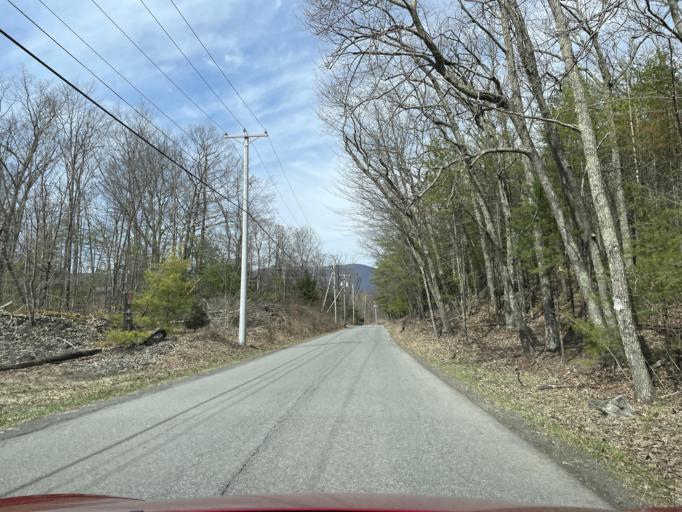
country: US
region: New York
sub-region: Ulster County
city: West Hurley
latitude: 42.0016
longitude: -74.0944
